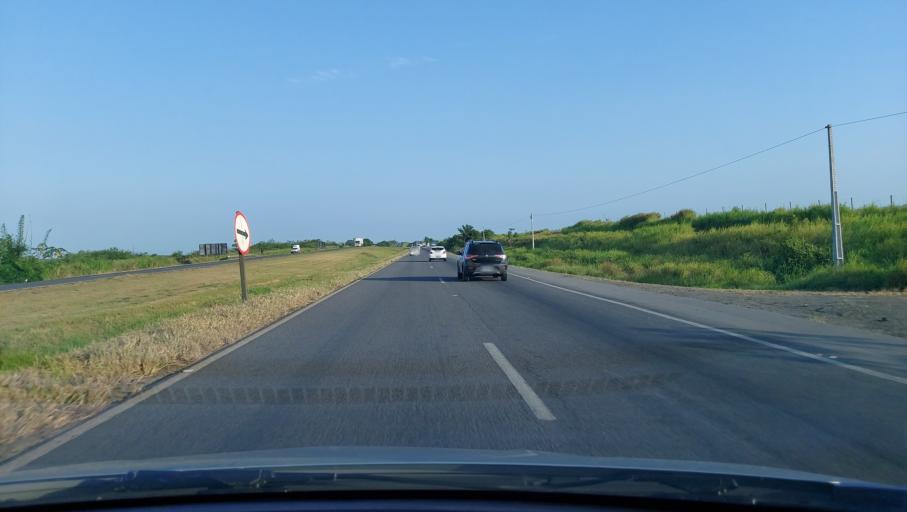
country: BR
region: Bahia
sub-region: Santo Amaro
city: Santo Amaro
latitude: -12.4966
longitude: -38.6481
